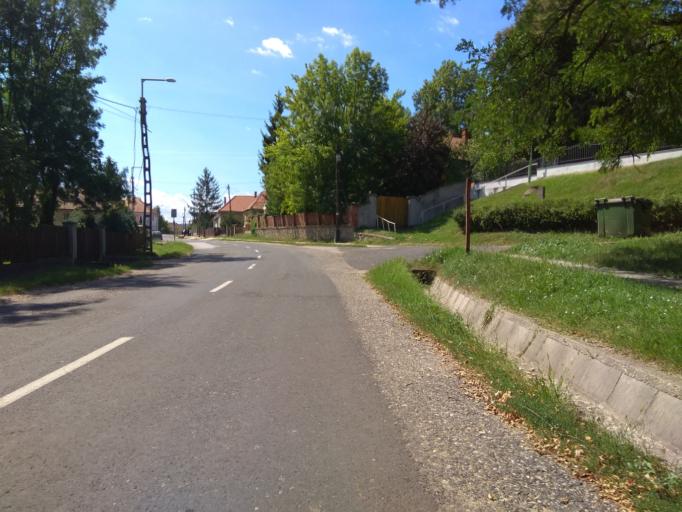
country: HU
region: Borsod-Abauj-Zemplen
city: Izsofalva
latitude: 48.2821
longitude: 20.6517
